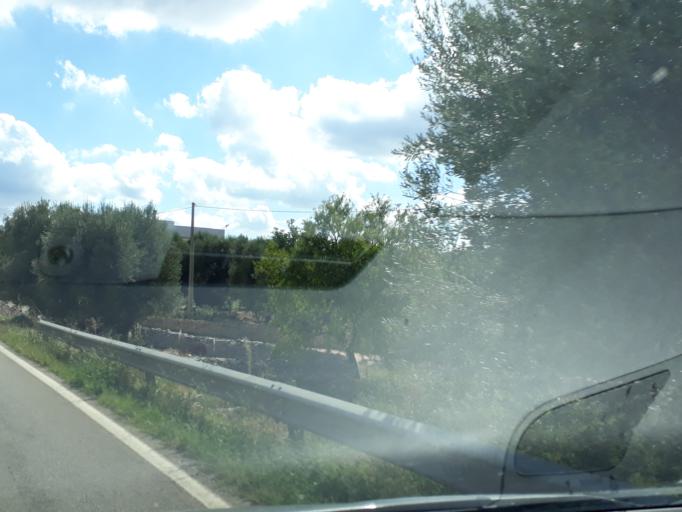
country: IT
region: Apulia
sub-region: Provincia di Brindisi
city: Fasano
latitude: 40.8232
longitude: 17.3729
